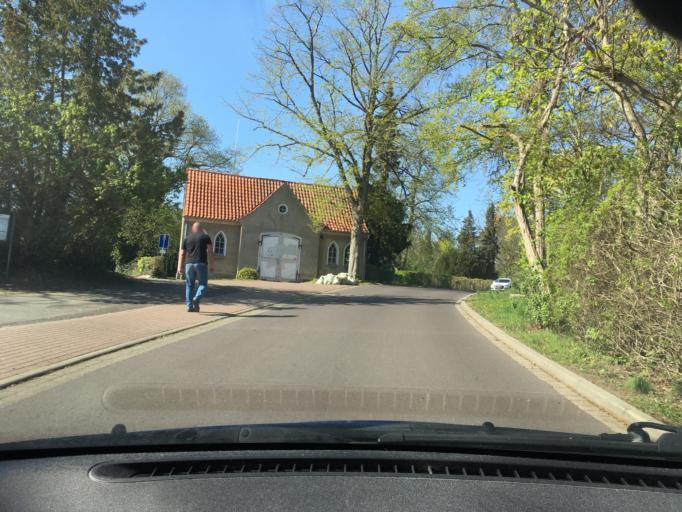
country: DE
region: Lower Saxony
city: Hitzacker
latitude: 53.1525
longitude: 11.0421
